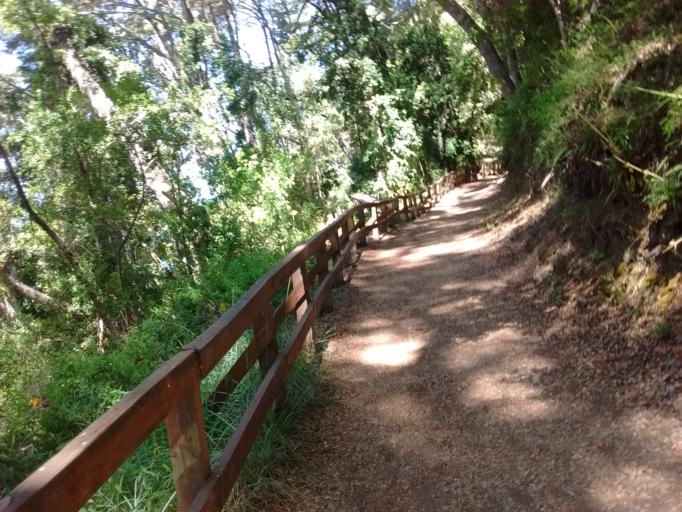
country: AR
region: Neuquen
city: Villa La Angostura
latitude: -40.7879
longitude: -71.6564
